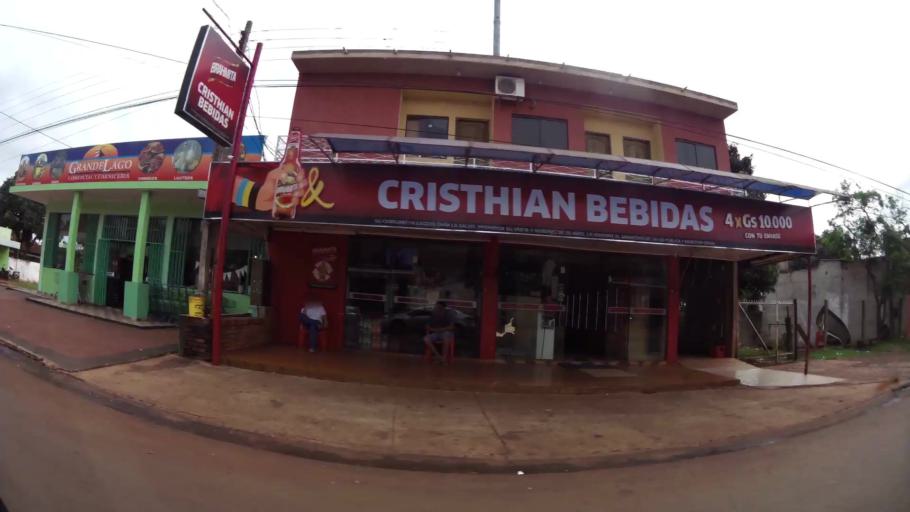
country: PY
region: Alto Parana
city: Ciudad del Este
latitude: -25.3941
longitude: -54.6408
